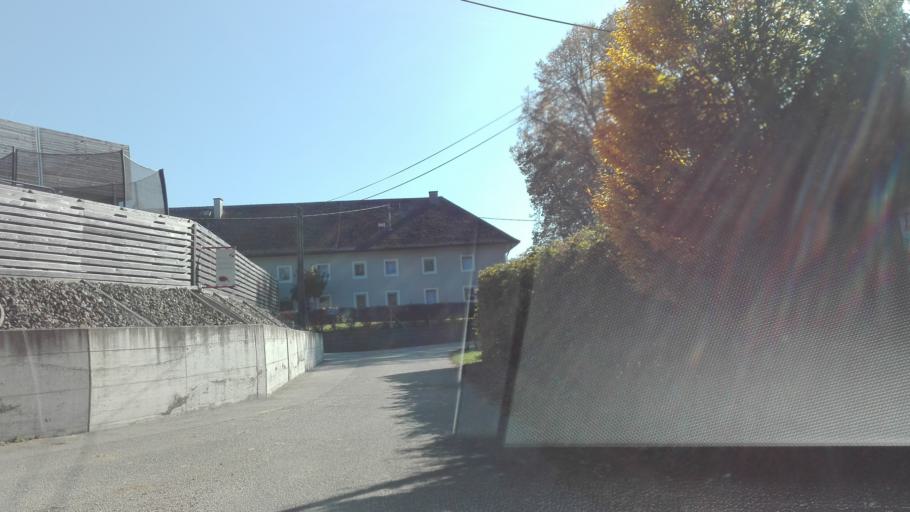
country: AT
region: Upper Austria
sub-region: Politischer Bezirk Urfahr-Umgebung
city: Ottensheim
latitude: 48.3054
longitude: 14.1767
